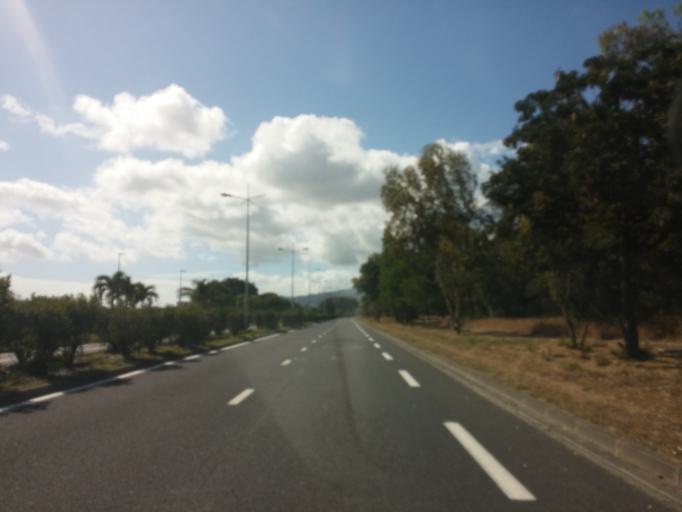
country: RE
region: Reunion
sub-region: Reunion
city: Le Port
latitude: -20.9515
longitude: 55.2978
